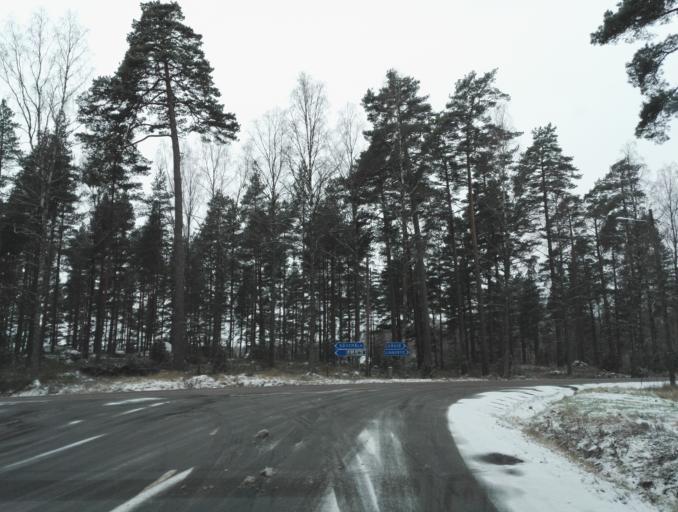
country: SE
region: Kronoberg
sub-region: Lessebo Kommun
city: Hovmantorp
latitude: 56.6600
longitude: 15.1422
